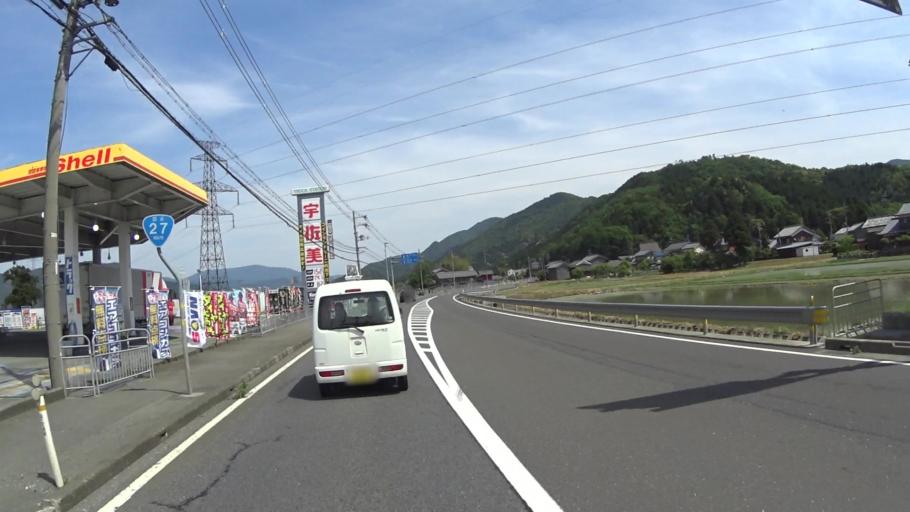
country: JP
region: Fukui
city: Obama
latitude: 35.4787
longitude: 135.7963
